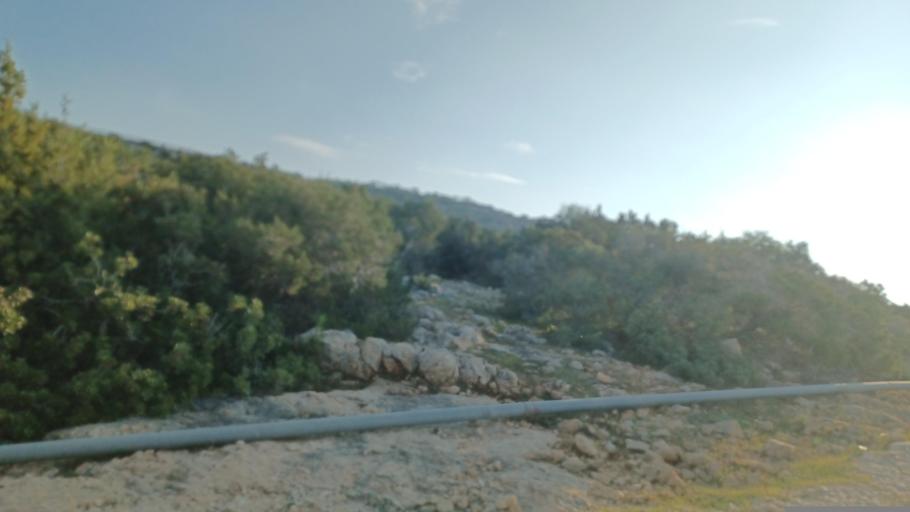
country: CY
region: Pafos
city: Pegeia
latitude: 34.8917
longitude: 32.3516
